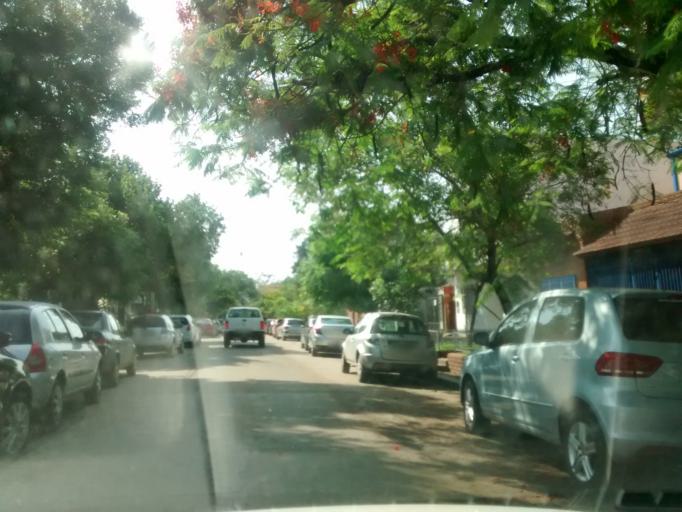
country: AR
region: Chaco
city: Resistencia
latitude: -27.4592
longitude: -58.9792
